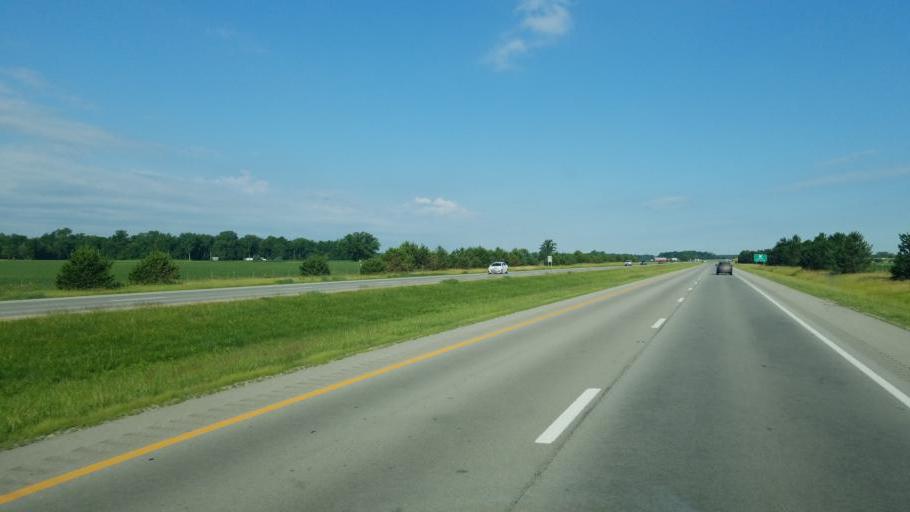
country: US
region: Ohio
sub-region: Wyandot County
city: Carey
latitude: 40.9638
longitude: -83.4709
